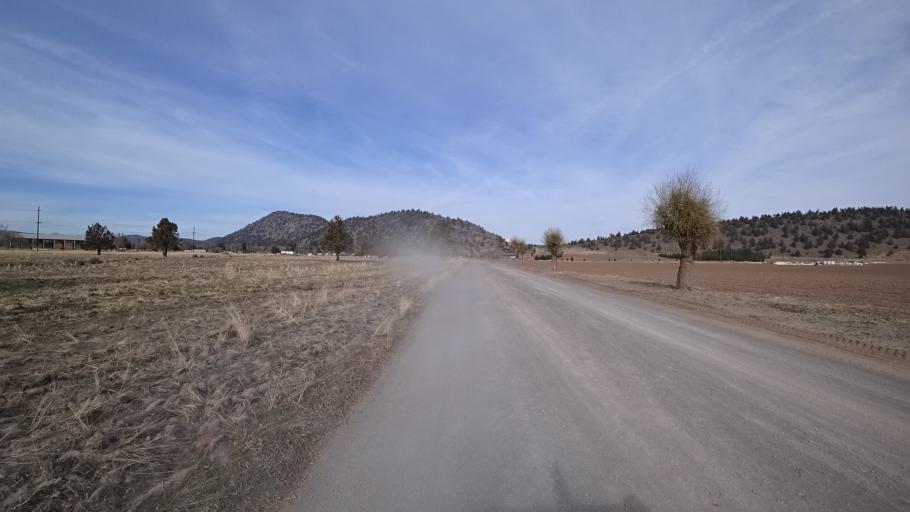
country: US
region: Oregon
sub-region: Klamath County
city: Klamath Falls
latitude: 41.9635
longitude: -121.9115
